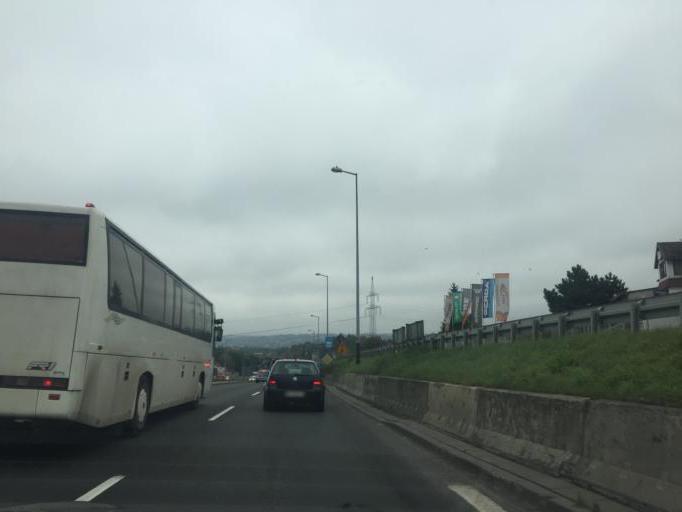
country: PL
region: Lesser Poland Voivodeship
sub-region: Powiat wielicki
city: Wieliczka
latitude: 50.0028
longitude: 20.0243
